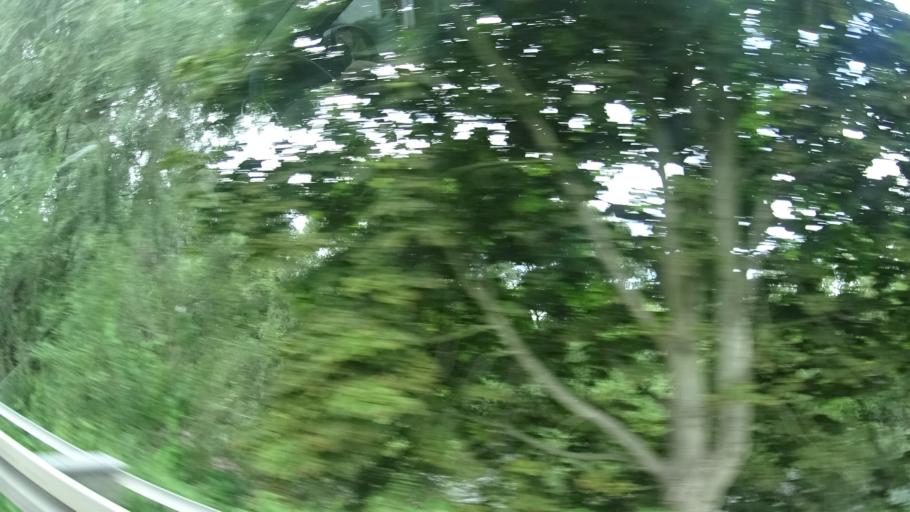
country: DE
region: Thuringia
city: Kaulsdorf
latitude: 50.6243
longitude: 11.4294
